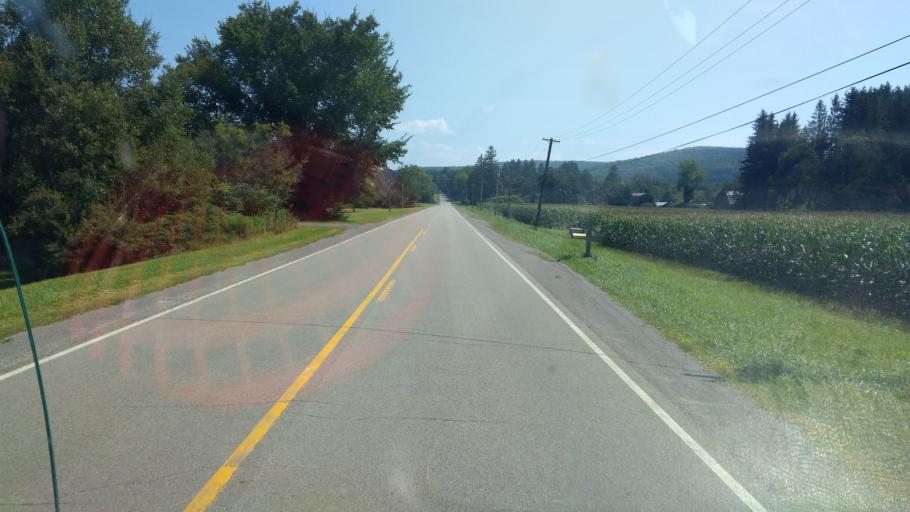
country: US
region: New York
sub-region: Allegany County
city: Belmont
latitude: 42.2998
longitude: -77.9838
